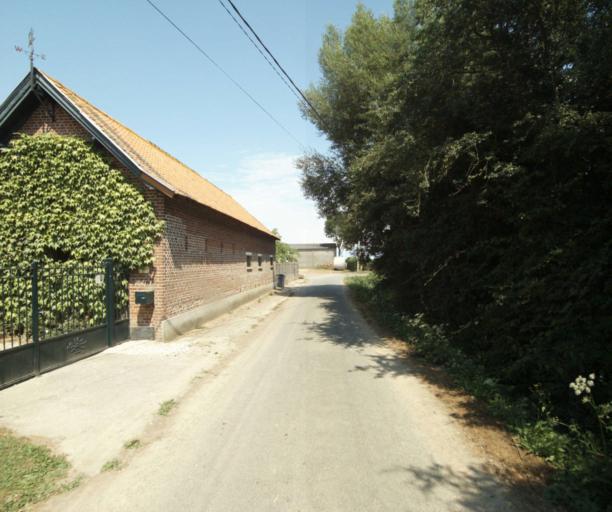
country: FR
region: Nord-Pas-de-Calais
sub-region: Departement du Nord
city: Quesnoy-sur-Deule
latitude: 50.7341
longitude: 2.9877
